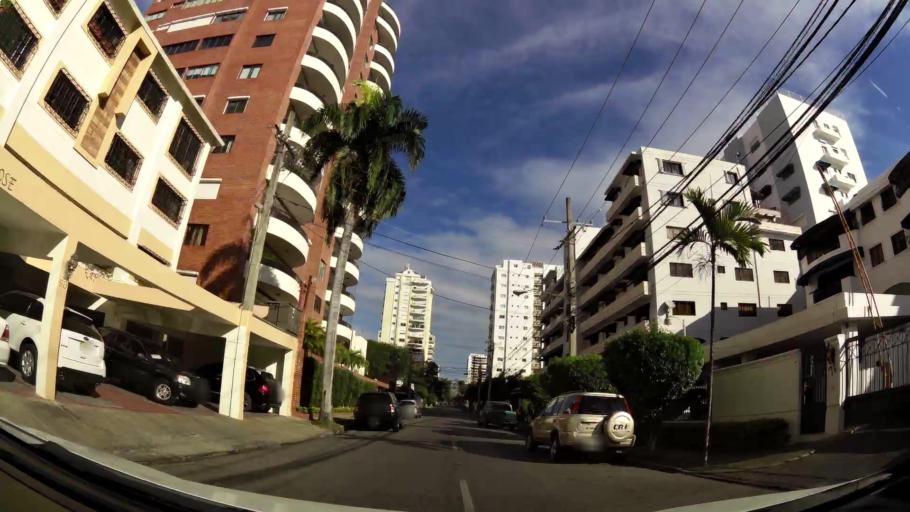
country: DO
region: Nacional
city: La Julia
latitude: 18.4770
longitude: -69.9392
